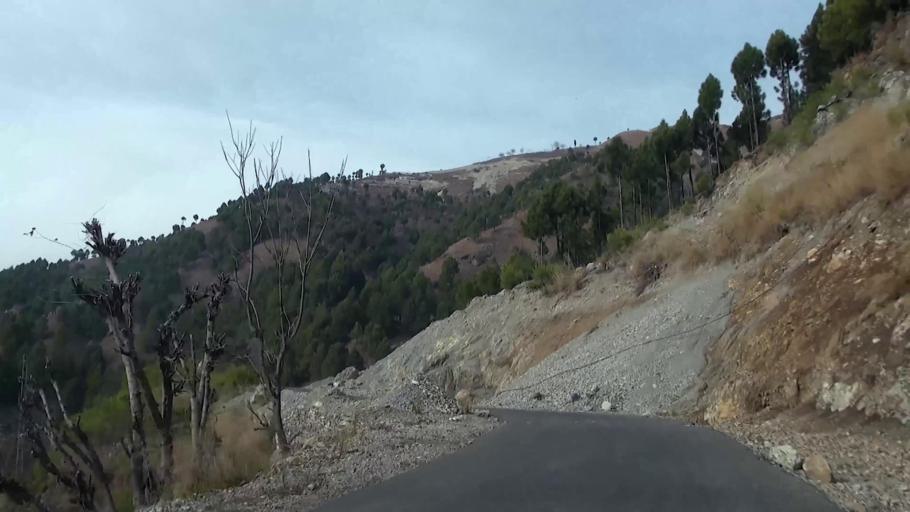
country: PK
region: Azad Kashmir
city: Muzaffarabad
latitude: 34.3654
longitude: 73.5008
